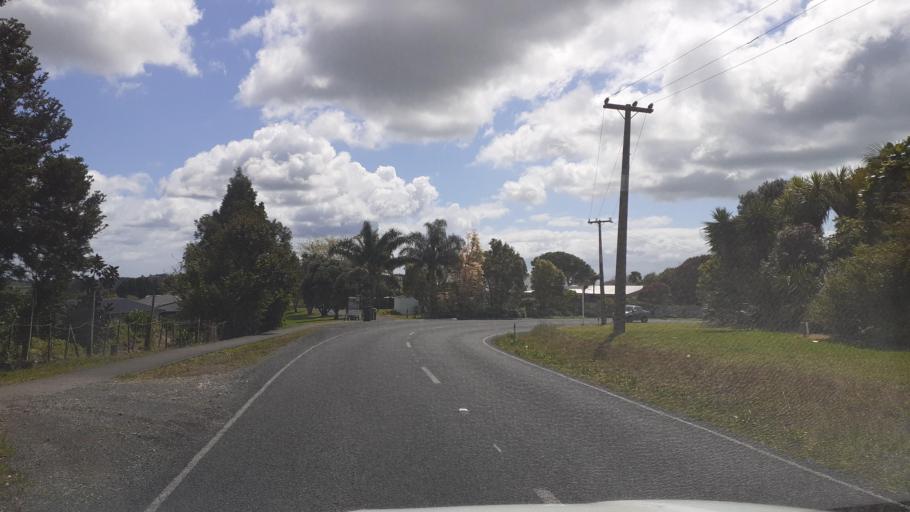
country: NZ
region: Northland
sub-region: Far North District
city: Kerikeri
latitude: -35.2183
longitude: 173.9787
